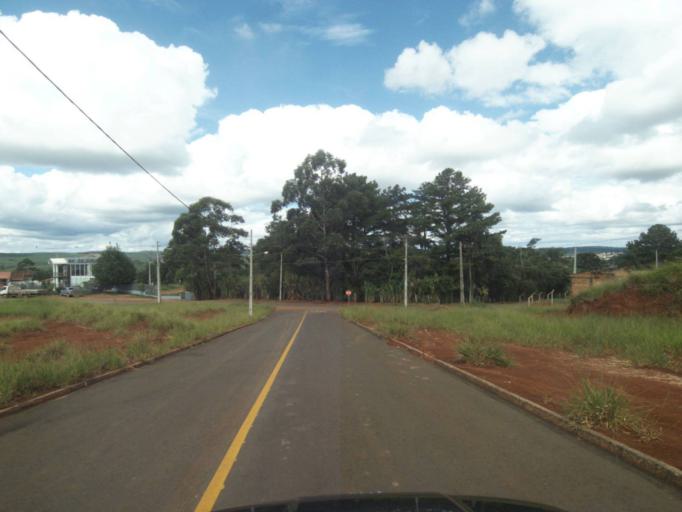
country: BR
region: Parana
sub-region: Telemaco Borba
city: Telemaco Borba
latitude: -24.3127
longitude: -50.6365
